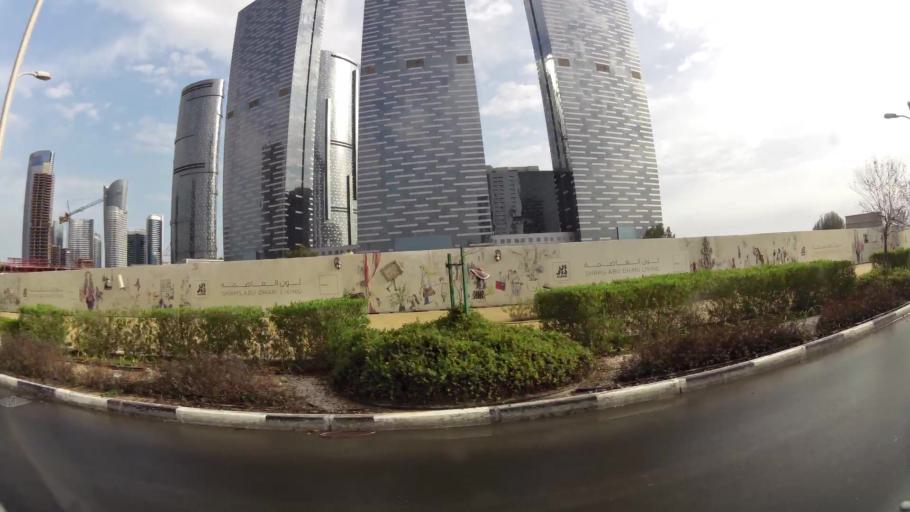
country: AE
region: Abu Dhabi
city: Abu Dhabi
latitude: 24.4919
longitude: 54.4071
